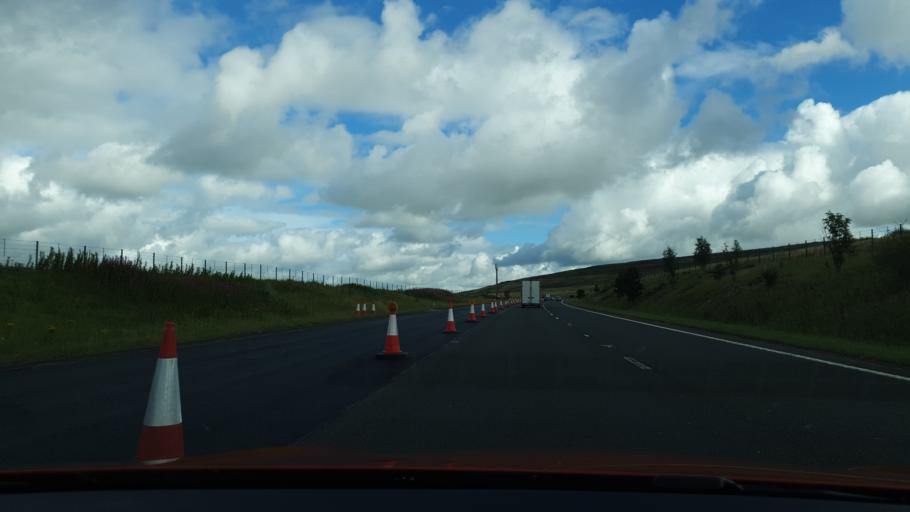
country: GB
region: England
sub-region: Cumbria
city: Appleby-in-Westmorland
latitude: 54.4775
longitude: -2.6349
